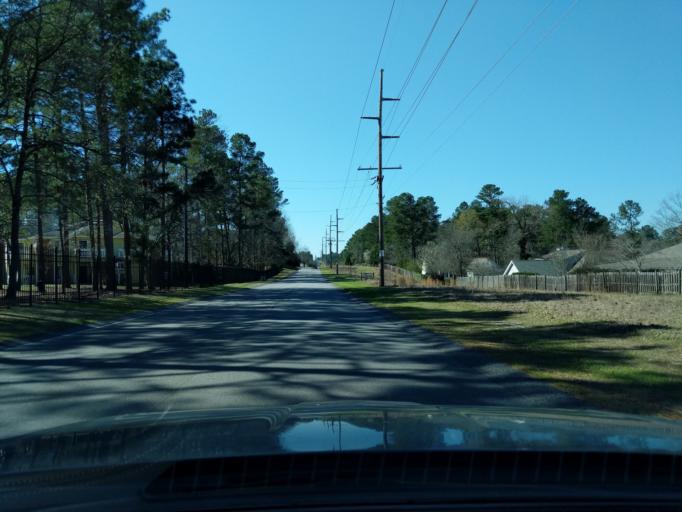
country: US
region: South Carolina
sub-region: Aiken County
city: Aiken
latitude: 33.5311
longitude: -81.7486
